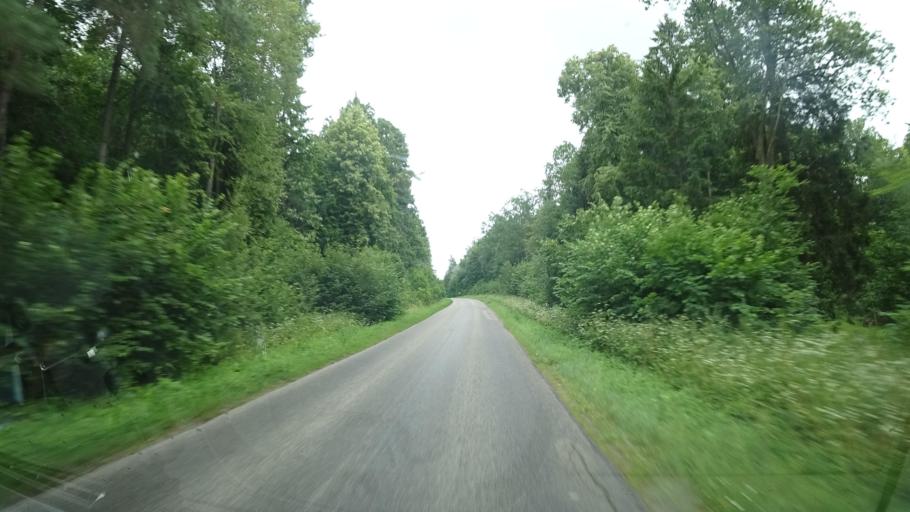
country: PL
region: Warmian-Masurian Voivodeship
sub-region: Powiat goldapski
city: Goldap
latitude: 54.3090
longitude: 22.3991
